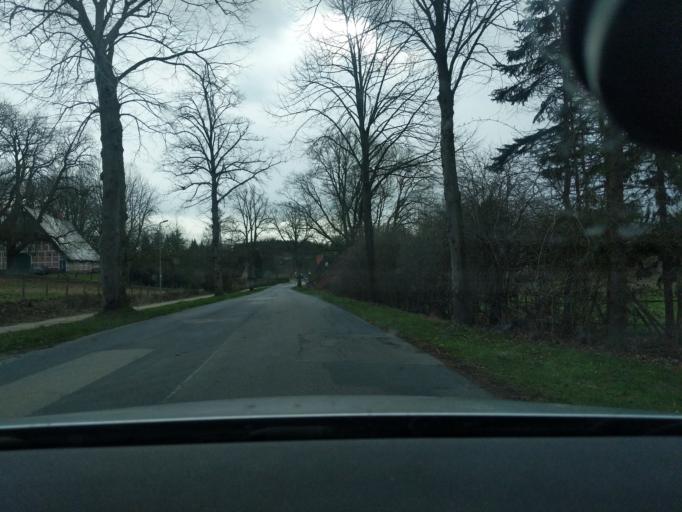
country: DE
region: Lower Saxony
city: Harsefeld
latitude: 53.4860
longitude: 9.5182
